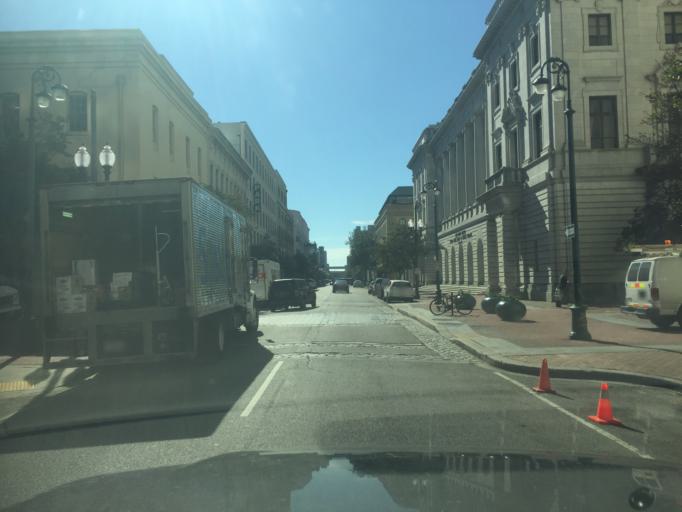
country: US
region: Louisiana
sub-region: Orleans Parish
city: New Orleans
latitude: 29.9481
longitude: -90.0684
